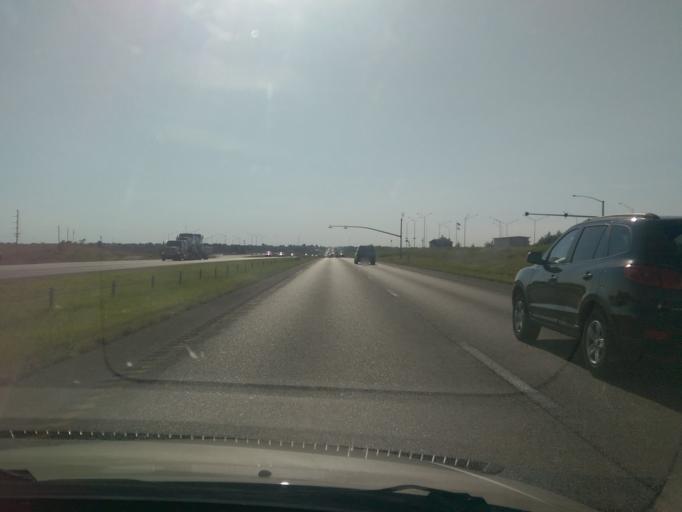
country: US
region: Missouri
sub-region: Lafayette County
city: Odessa
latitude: 39.0042
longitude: -93.8481
